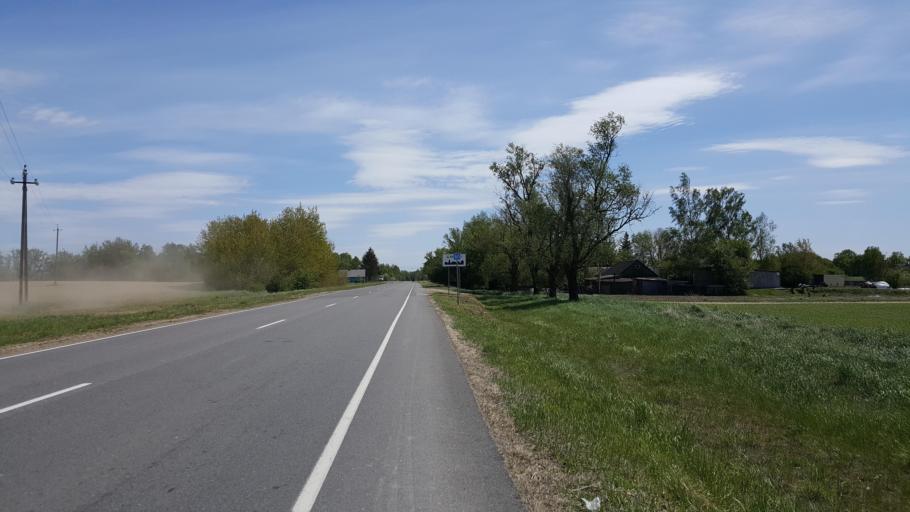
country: BY
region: Brest
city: Kobryn
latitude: 52.3545
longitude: 24.1804
